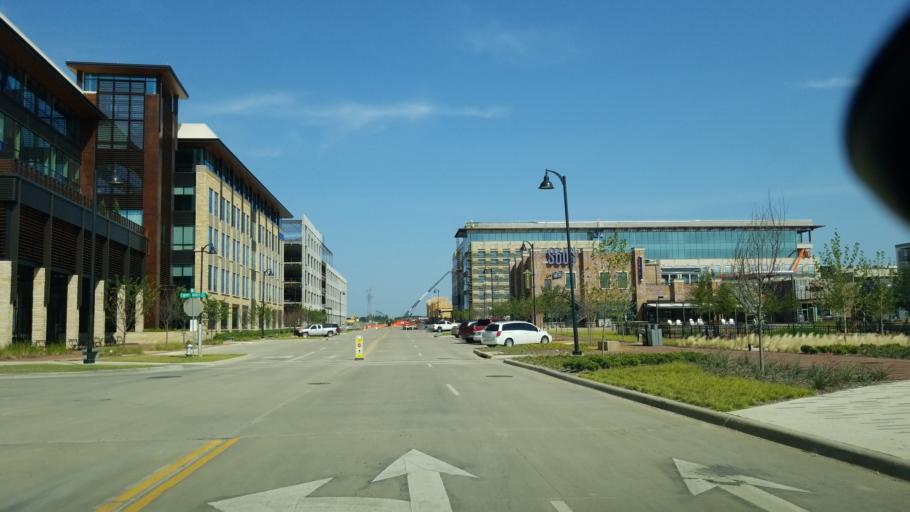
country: US
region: Texas
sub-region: Dallas County
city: Coppell
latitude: 32.9354
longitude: -96.9829
